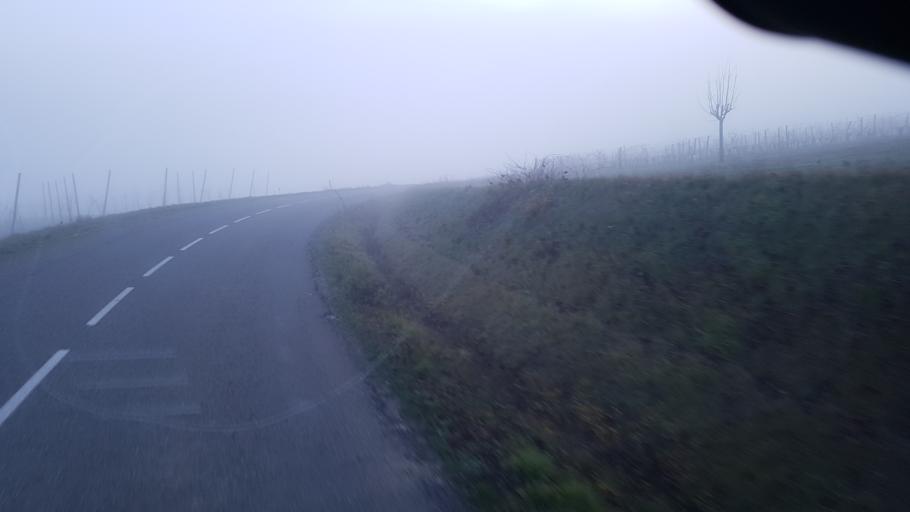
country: FR
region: Midi-Pyrenees
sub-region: Departement du Tarn-et-Garonne
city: Caussade
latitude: 44.2120
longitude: 1.5155
